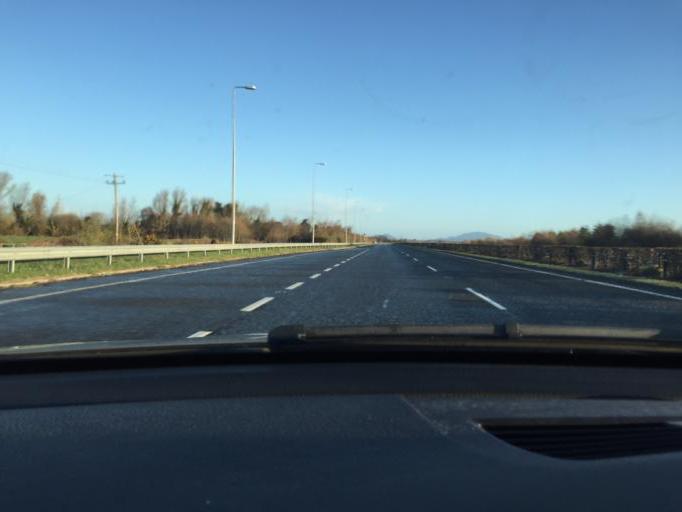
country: IE
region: Leinster
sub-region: Lu
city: Dromiskin
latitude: 53.9362
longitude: -6.4157
